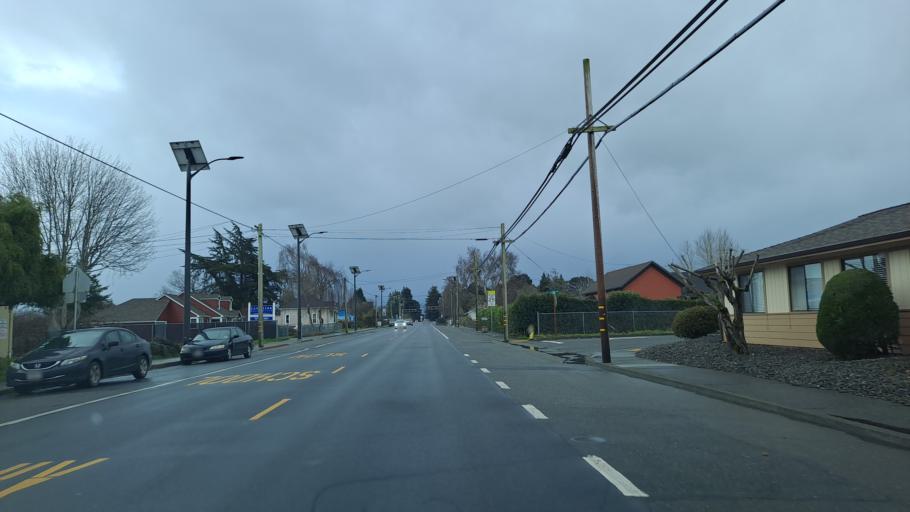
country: US
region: California
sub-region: Humboldt County
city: Fortuna
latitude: 40.5925
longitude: -124.1546
